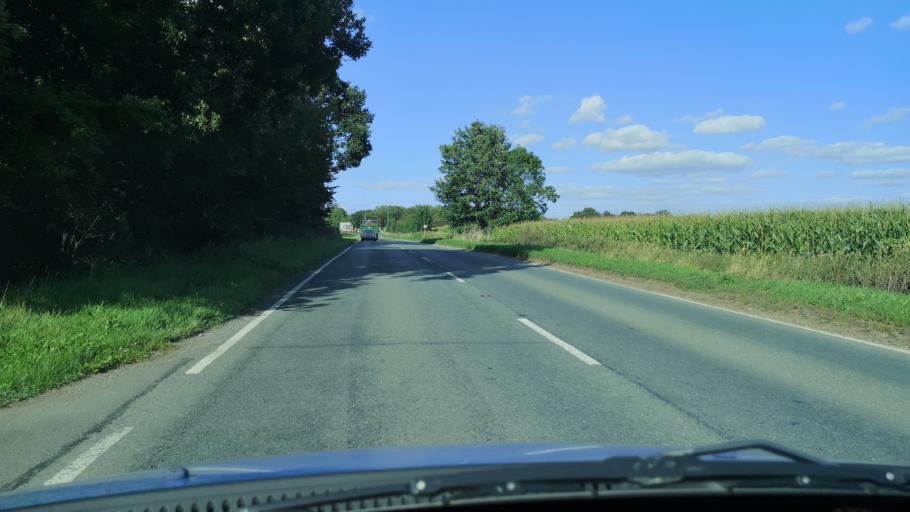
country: GB
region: England
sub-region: North Lincolnshire
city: Crowle
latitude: 53.5824
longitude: -0.8204
